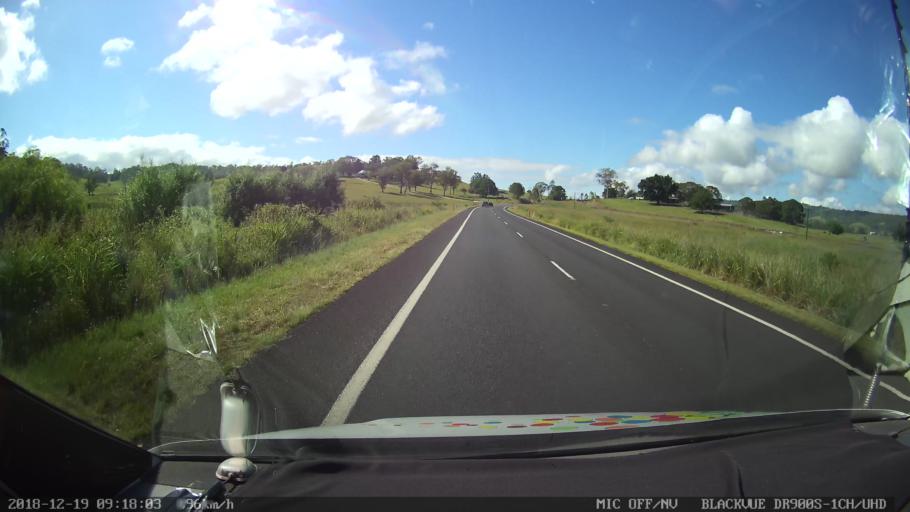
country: AU
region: New South Wales
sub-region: Kyogle
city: Kyogle
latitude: -28.5423
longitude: 152.9761
